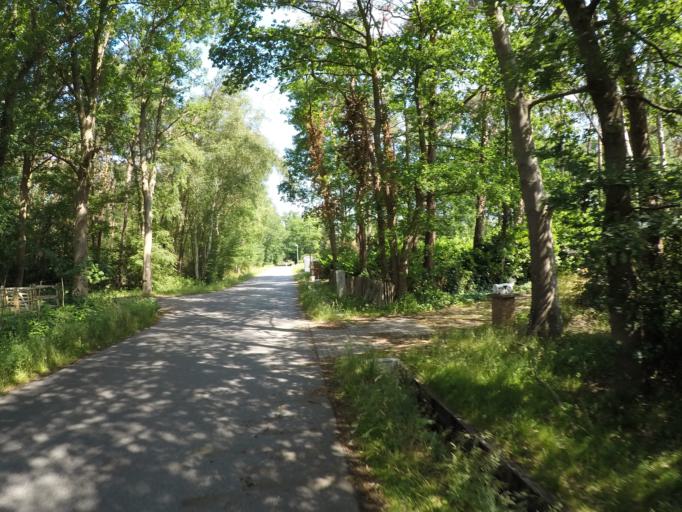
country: BE
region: Flanders
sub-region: Provincie Antwerpen
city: Zandhoven
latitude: 51.2410
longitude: 4.6300
